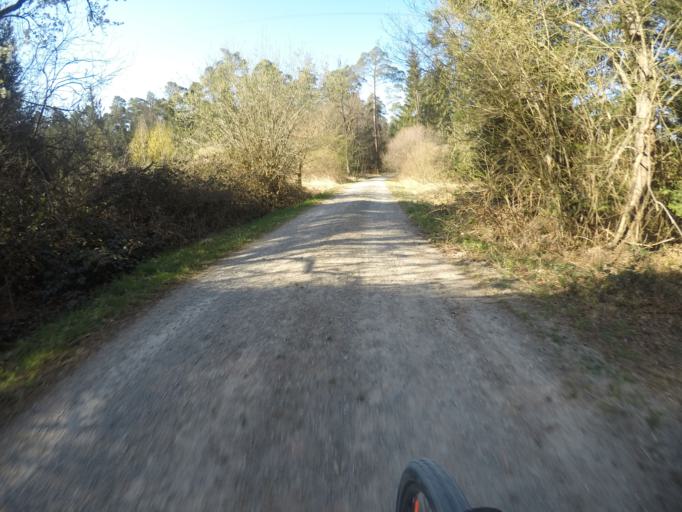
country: DE
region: Baden-Wuerttemberg
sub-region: Tuebingen Region
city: Dettenhausen
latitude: 48.6055
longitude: 9.1259
